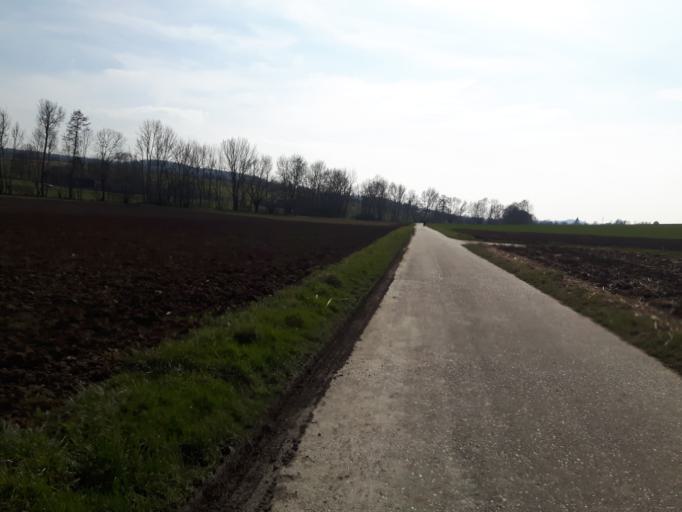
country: DE
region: Baden-Wuerttemberg
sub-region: Regierungsbezirk Stuttgart
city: Schwaigern
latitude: 49.1371
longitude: 9.0235
